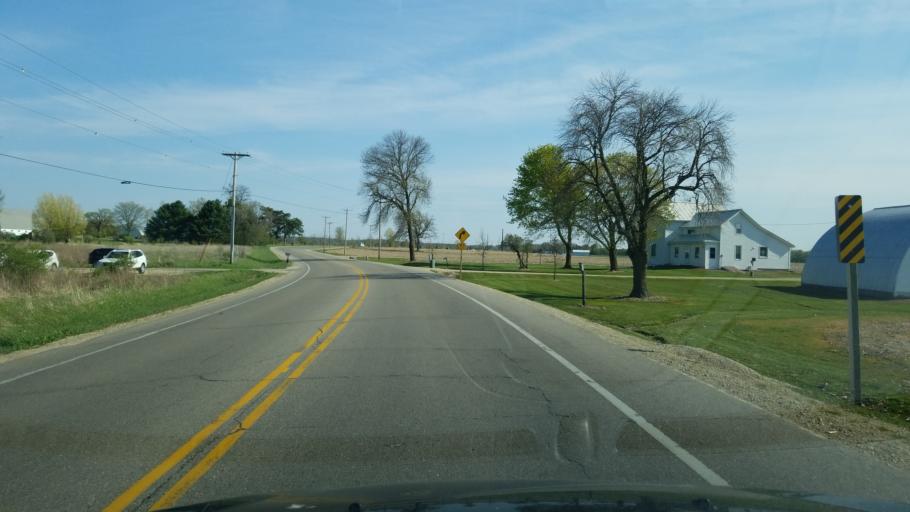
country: US
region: Wisconsin
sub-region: Dane County
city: Fitchburg
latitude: 42.9426
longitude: -89.4387
